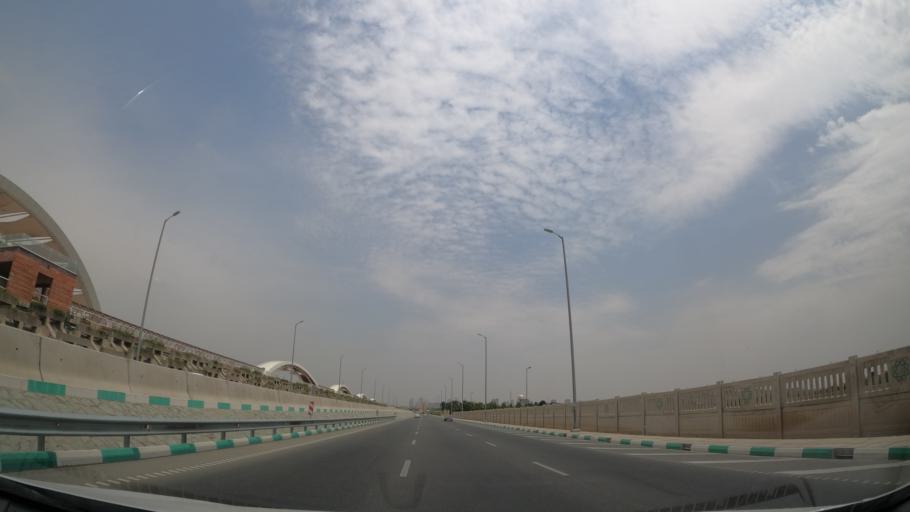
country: IR
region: Tehran
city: Shahr-e Qods
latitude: 35.7396
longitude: 51.2140
